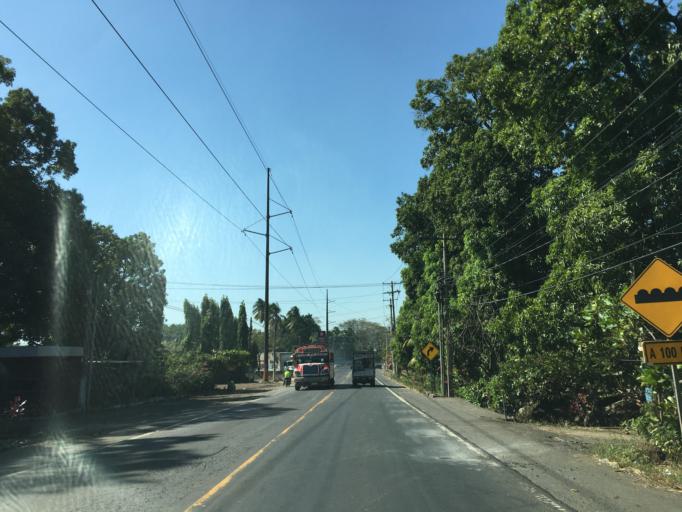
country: GT
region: Escuintla
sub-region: Municipio de Escuintla
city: Escuintla
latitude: 14.2713
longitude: -90.7921
